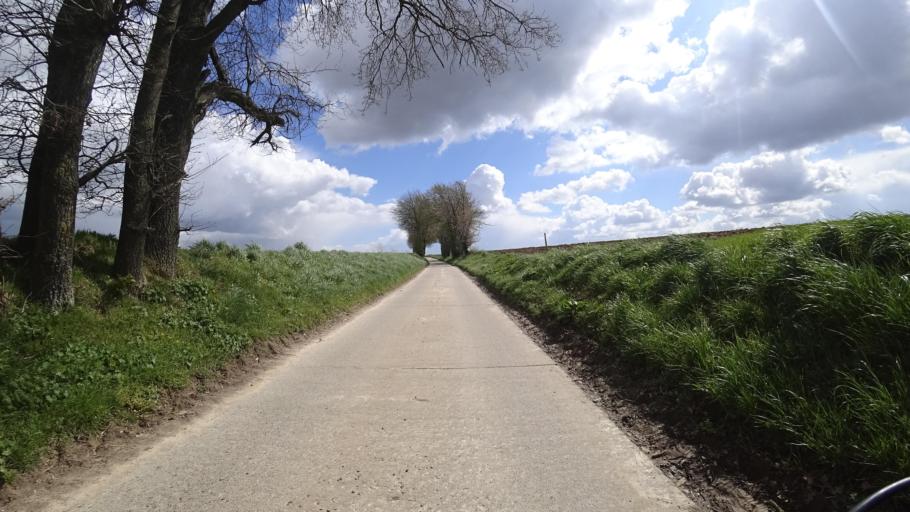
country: BE
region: Wallonia
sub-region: Province du Brabant Wallon
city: Walhain-Saint-Paul
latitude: 50.6585
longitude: 4.6856
